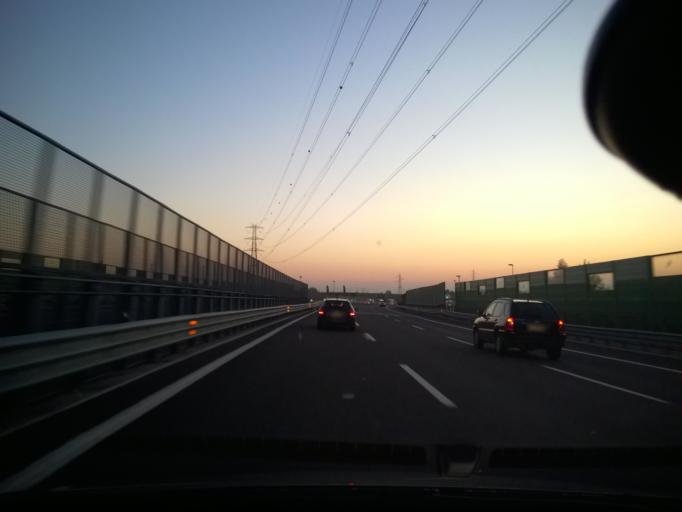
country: IT
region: Veneto
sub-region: Provincia di Venezia
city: Marano
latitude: 45.4788
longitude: 12.1293
